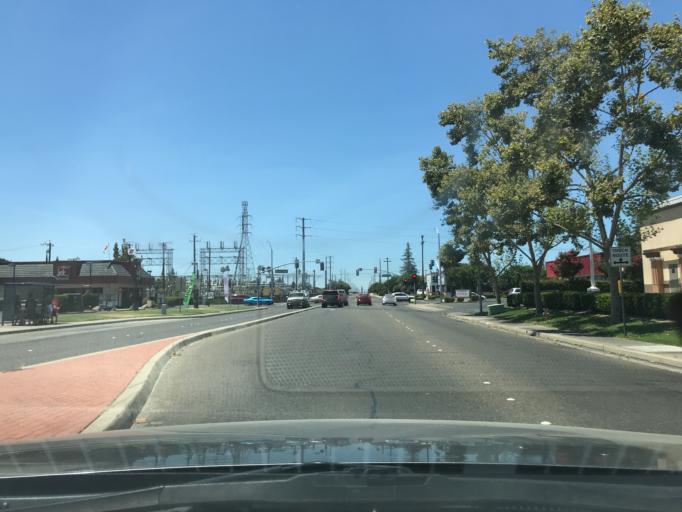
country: US
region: California
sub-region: Merced County
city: Atwater
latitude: 37.3604
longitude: -120.6128
